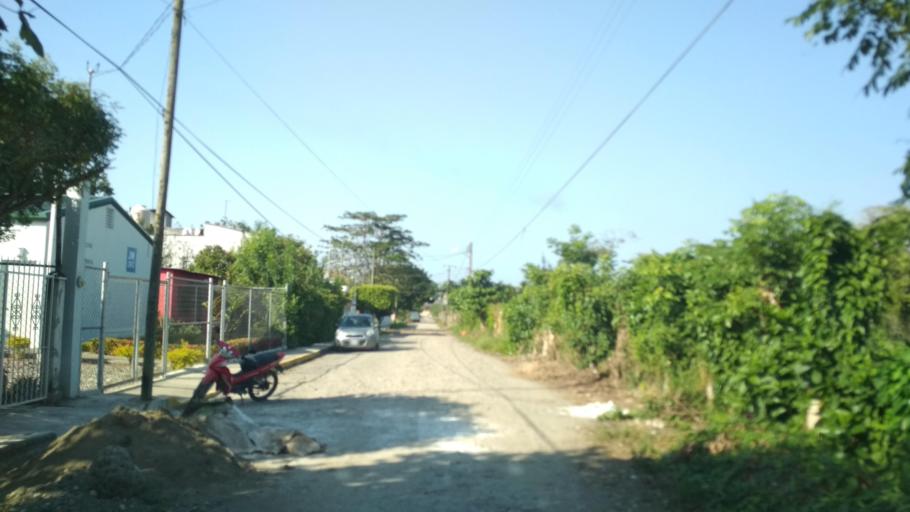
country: MX
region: Veracruz
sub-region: Martinez de la Torre
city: El Progreso
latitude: 20.0827
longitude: -97.0217
